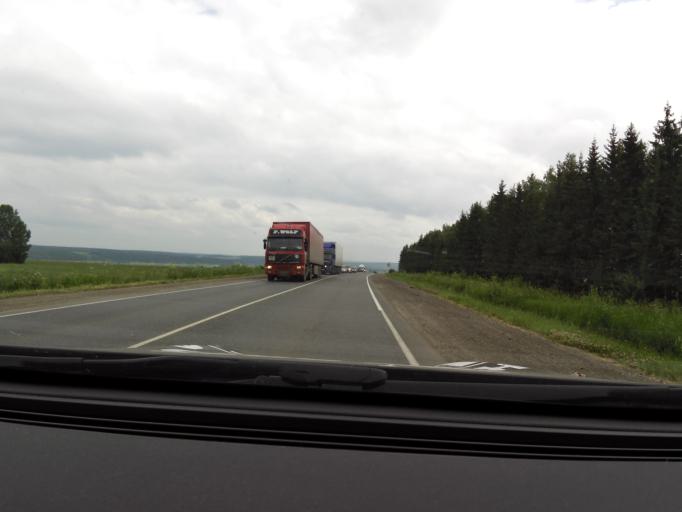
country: RU
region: Perm
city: Kungur
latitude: 57.4763
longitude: 56.7330
